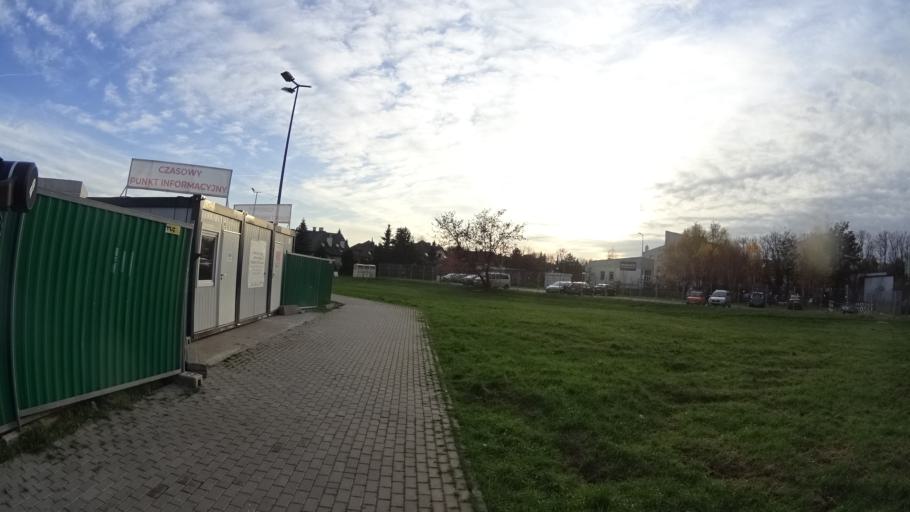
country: PL
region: Masovian Voivodeship
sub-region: Warszawa
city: Targowek
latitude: 52.2899
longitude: 21.0580
